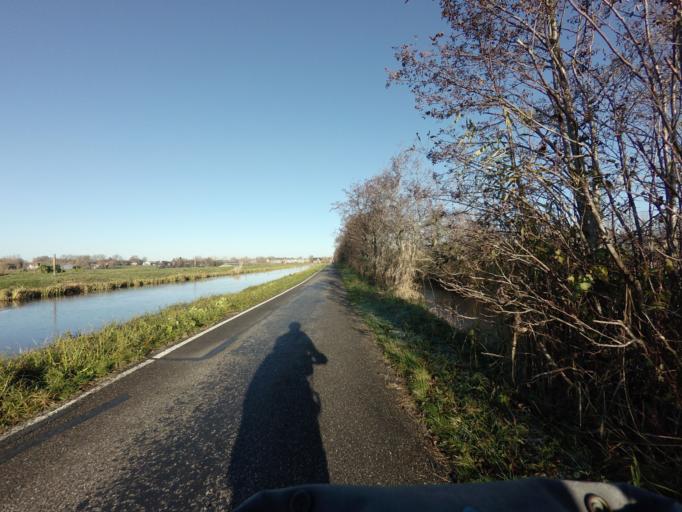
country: NL
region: Utrecht
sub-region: Gemeente De Ronde Venen
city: Mijdrecht
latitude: 52.1898
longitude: 4.9049
